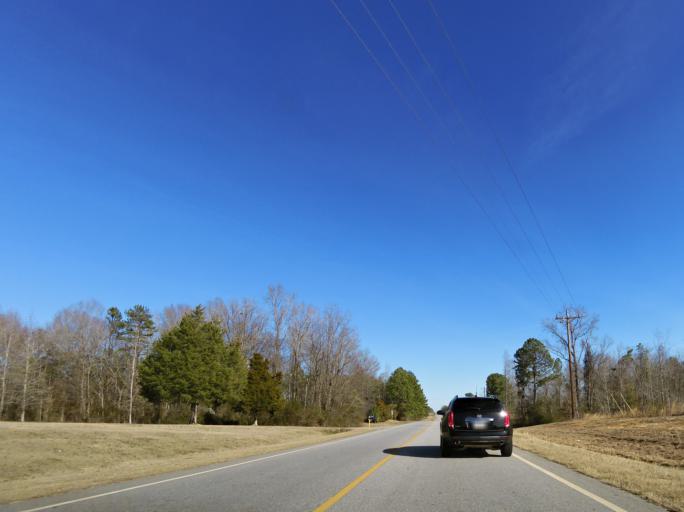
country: US
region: Georgia
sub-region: Crawford County
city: Roberta
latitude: 32.7527
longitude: -84.1881
